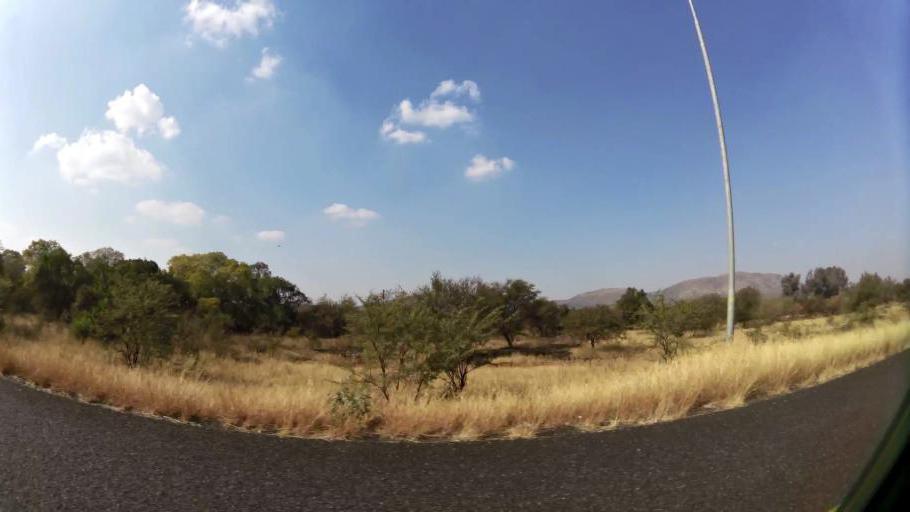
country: ZA
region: North-West
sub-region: Bojanala Platinum District Municipality
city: Rustenburg
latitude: -25.6274
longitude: 27.1578
